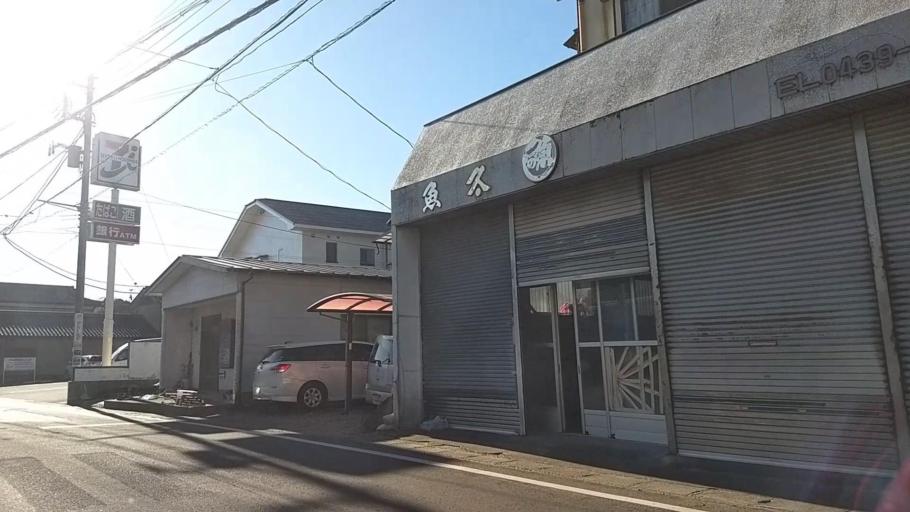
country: JP
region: Chiba
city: Futtsu
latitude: 35.2807
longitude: 139.8545
